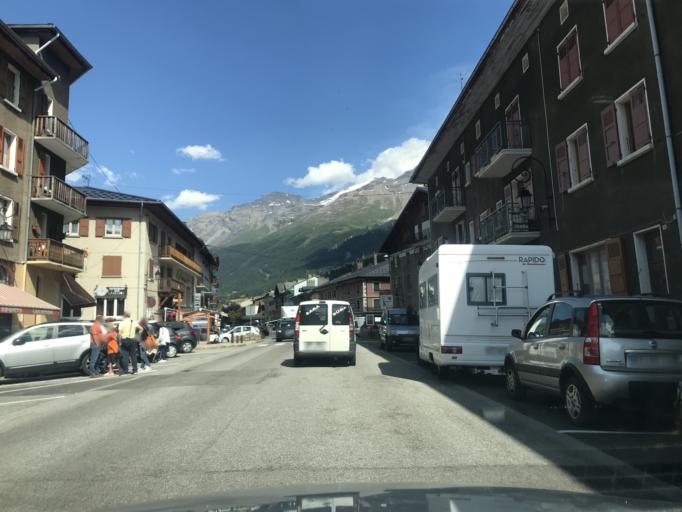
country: IT
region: Piedmont
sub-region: Provincia di Torino
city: Moncenisio
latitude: 45.2853
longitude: 6.8761
